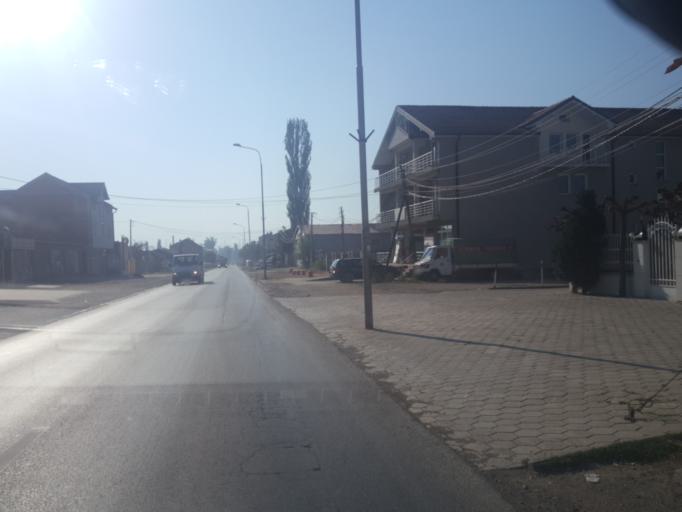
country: XK
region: Gjakova
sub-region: Komuna e Gjakoves
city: Gjakove
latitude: 42.4033
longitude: 20.4123
